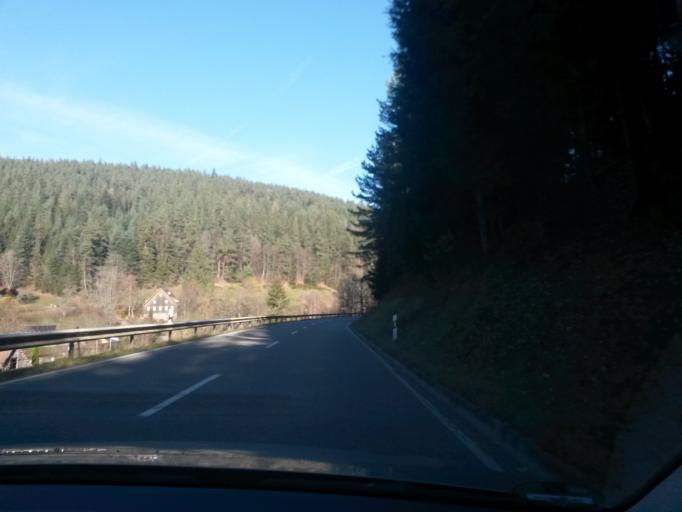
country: DE
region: Baden-Wuerttemberg
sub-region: Karlsruhe Region
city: Neuweiler
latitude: 48.6638
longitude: 8.5475
